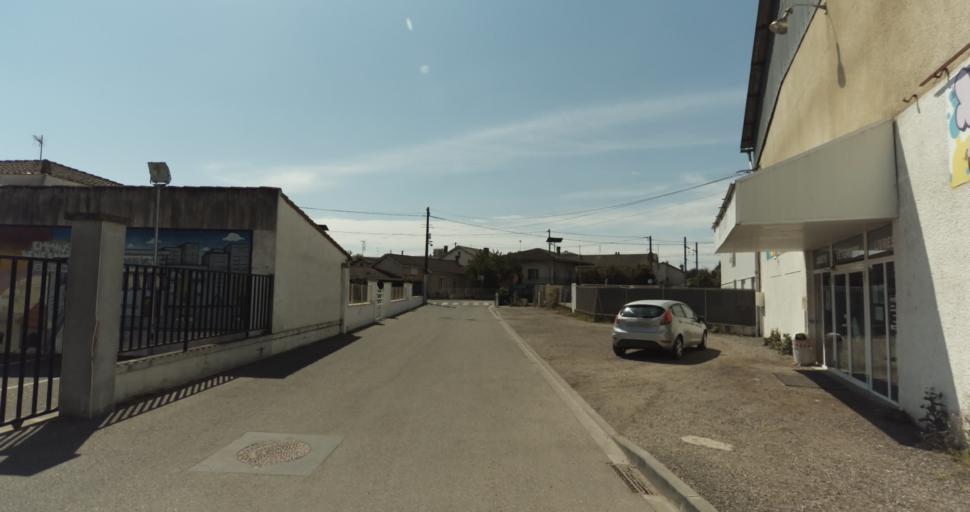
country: FR
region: Aquitaine
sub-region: Departement du Lot-et-Garonne
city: Agen
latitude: 44.2036
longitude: 0.6367
